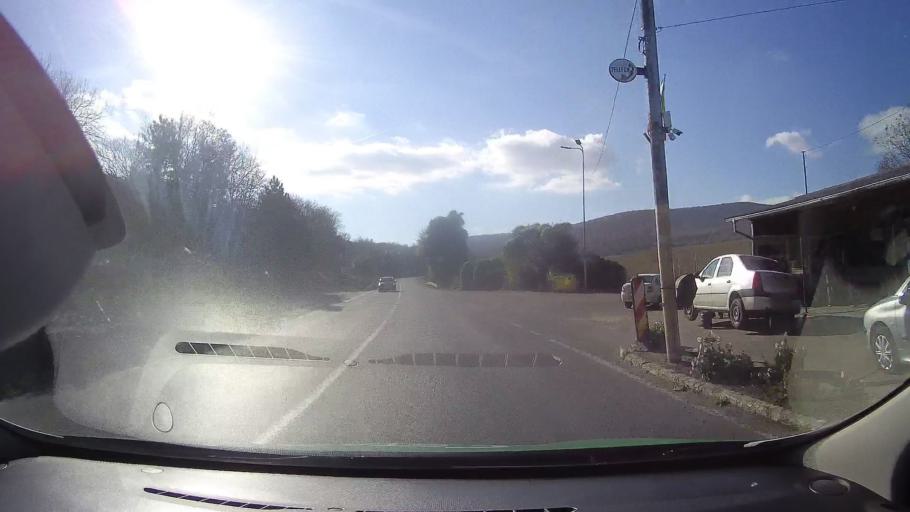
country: RO
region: Tulcea
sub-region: Oras Babadag
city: Babadag
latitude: 44.8788
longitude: 28.6920
